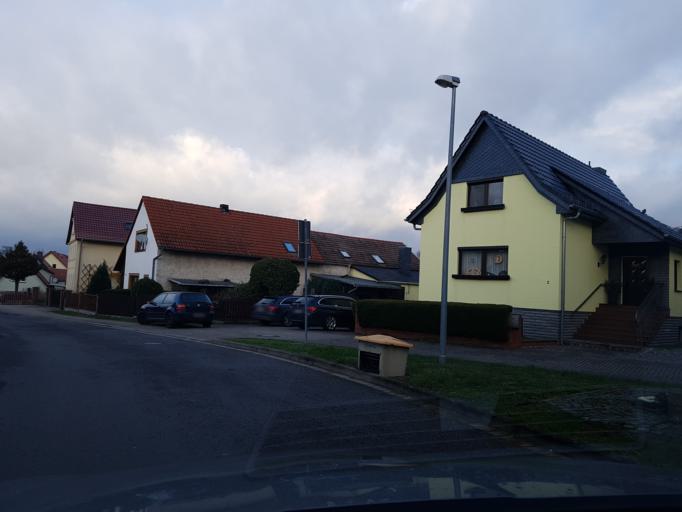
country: DE
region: Brandenburg
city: Merzdorf
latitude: 51.4025
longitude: 13.5342
